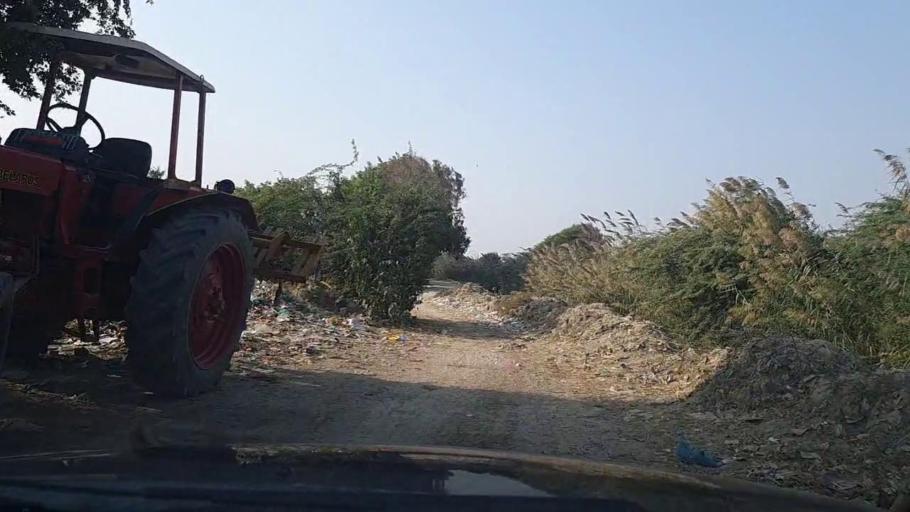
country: PK
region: Sindh
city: Mirpur Sakro
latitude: 24.6349
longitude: 67.7533
